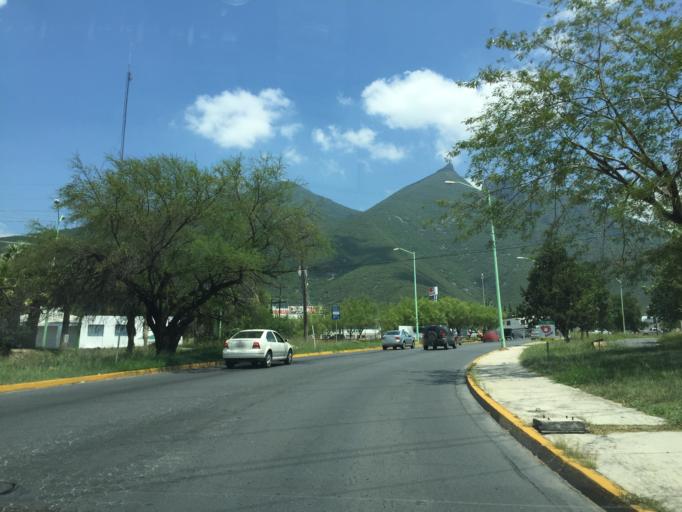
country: MX
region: Nuevo Leon
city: Guadalupe
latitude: 25.6474
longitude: -100.2690
